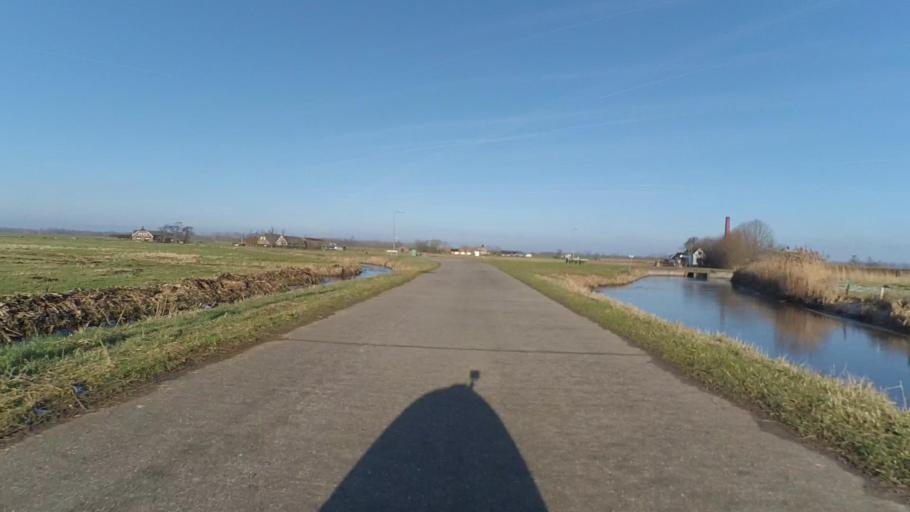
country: NL
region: Gelderland
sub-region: Gemeente Nijkerk
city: Nijkerk
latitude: 52.2599
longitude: 5.4951
